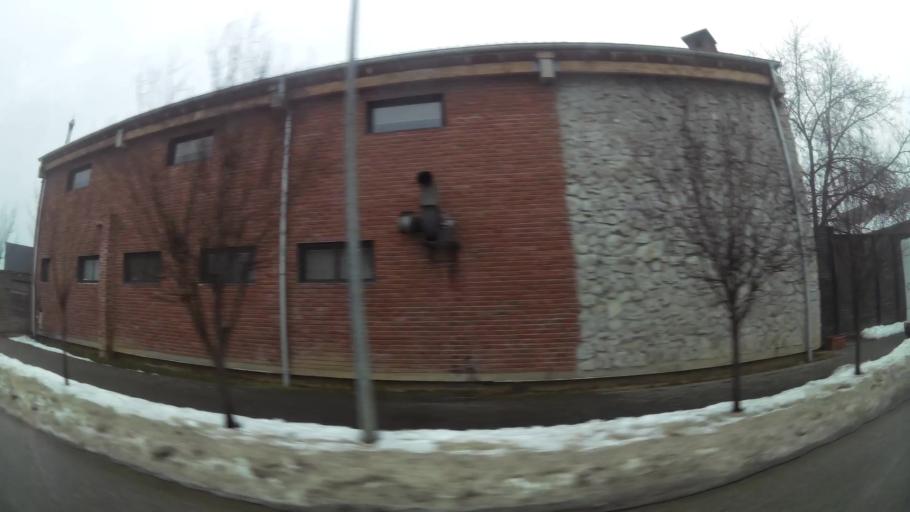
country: XK
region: Pristina
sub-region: Komuna e Prishtines
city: Pristina
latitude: 42.6489
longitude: 21.1490
